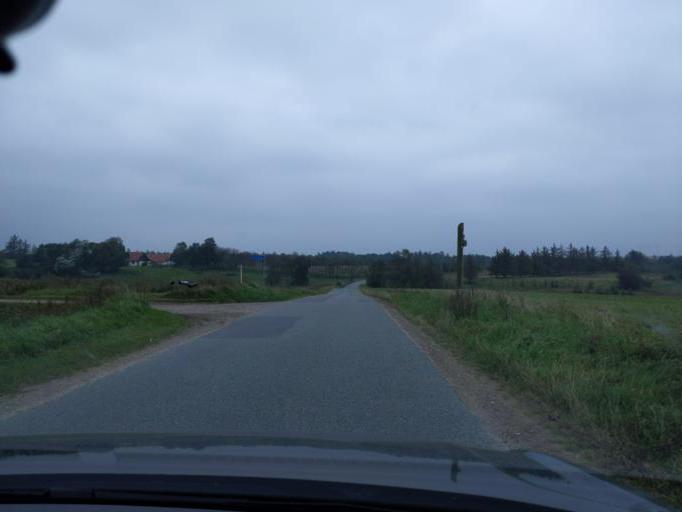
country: DK
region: Central Jutland
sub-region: Viborg Kommune
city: Stoholm
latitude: 56.5018
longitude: 9.2464
